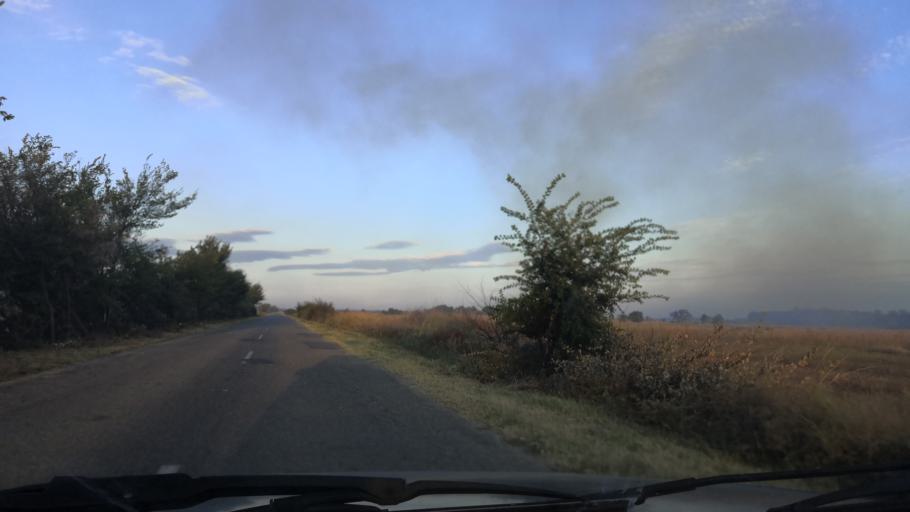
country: RS
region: Central Serbia
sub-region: Borski Okrug
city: Negotin
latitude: 44.2506
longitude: 22.5919
